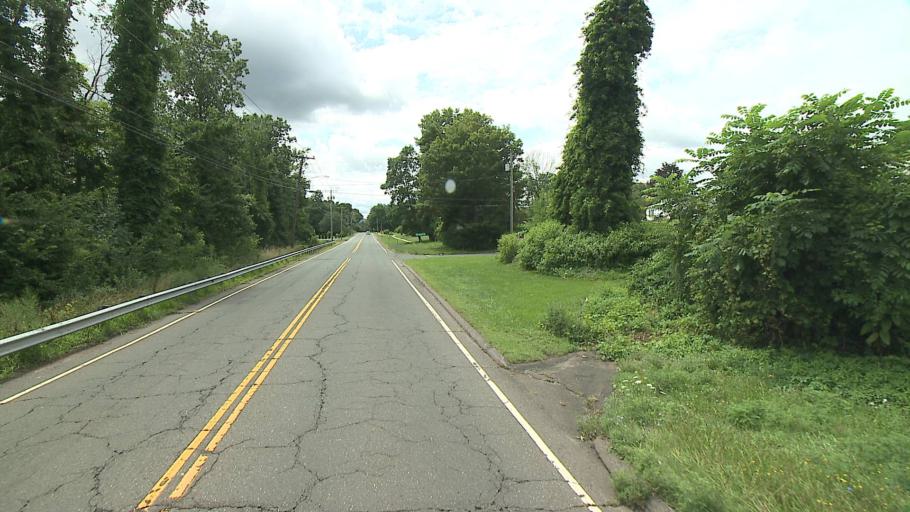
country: US
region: Connecticut
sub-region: Hartford County
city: Kensington
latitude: 41.6339
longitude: -72.7895
